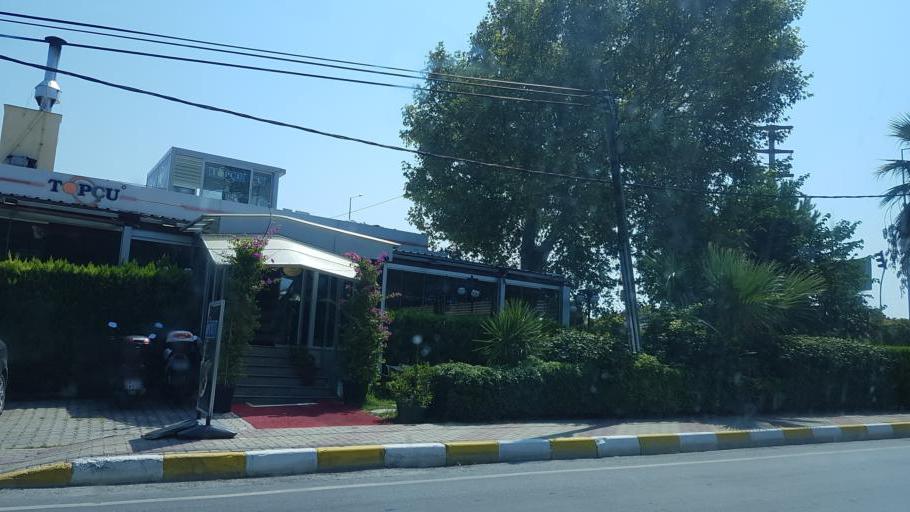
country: TR
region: Izmir
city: Urla
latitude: 38.3362
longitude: 26.7692
